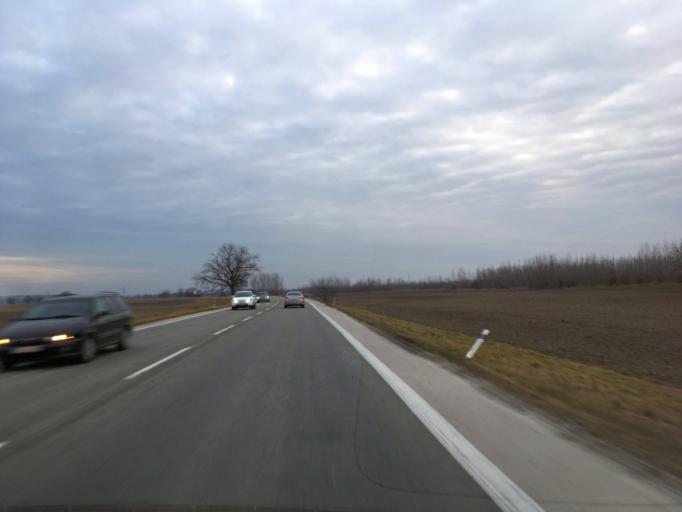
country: SK
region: Trnavsky
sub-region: Okres Dunajska Streda
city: Velky Meder
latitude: 47.9303
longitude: 17.7235
